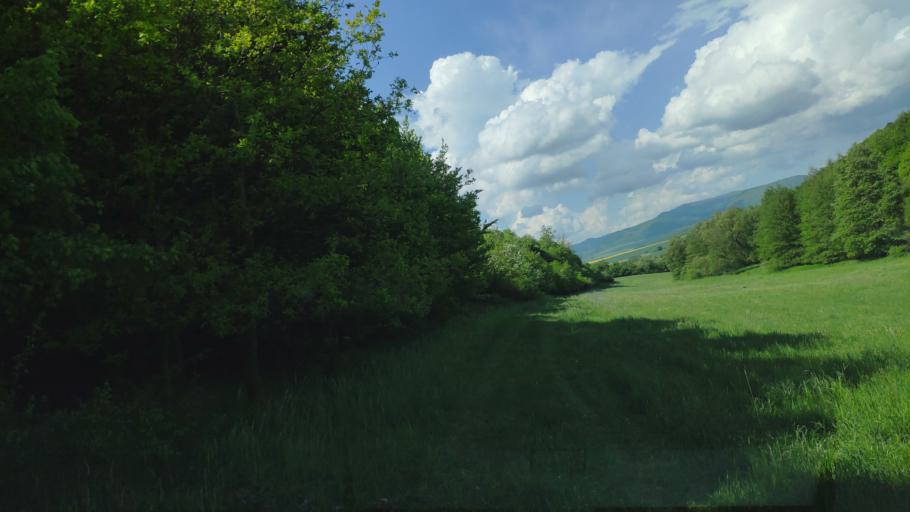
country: SK
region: Presovsky
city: Sabinov
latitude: 49.0517
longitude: 21.1600
